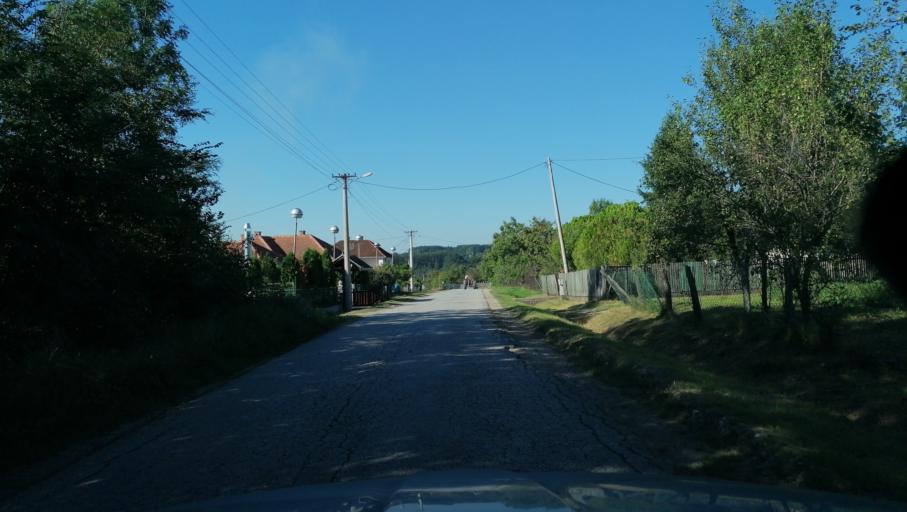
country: RS
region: Central Serbia
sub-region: Sumadijski Okrug
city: Knic
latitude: 43.8777
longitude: 20.6123
